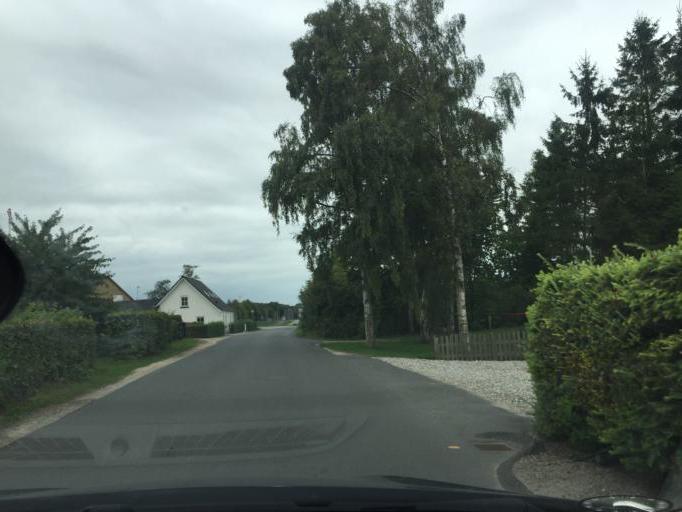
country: DK
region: South Denmark
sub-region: Assens Kommune
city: Arup
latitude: 55.3790
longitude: 10.0655
